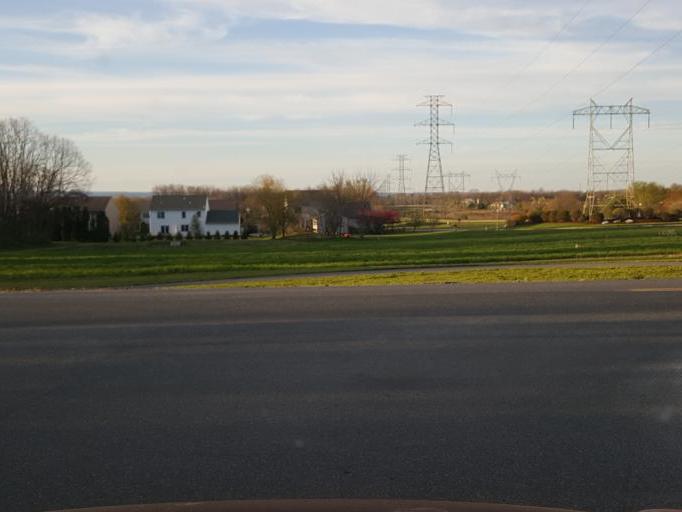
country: US
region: Pennsylvania
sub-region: Dauphin County
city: Hummelstown
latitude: 40.2386
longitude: -76.7176
